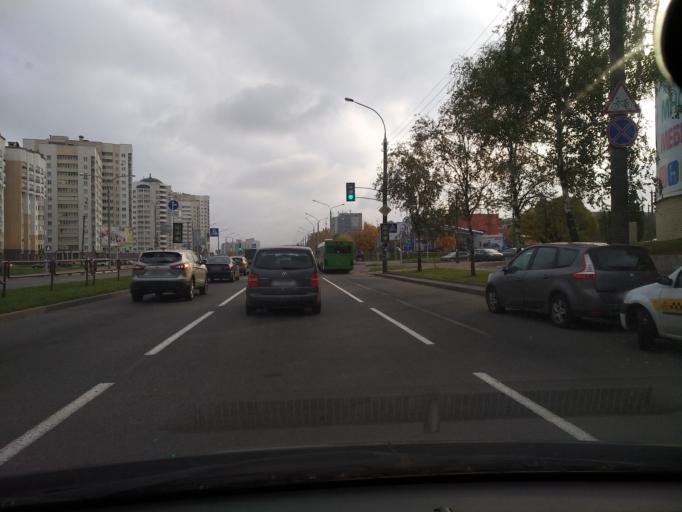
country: BY
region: Minsk
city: Novoye Medvezhino
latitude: 53.9173
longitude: 27.4548
